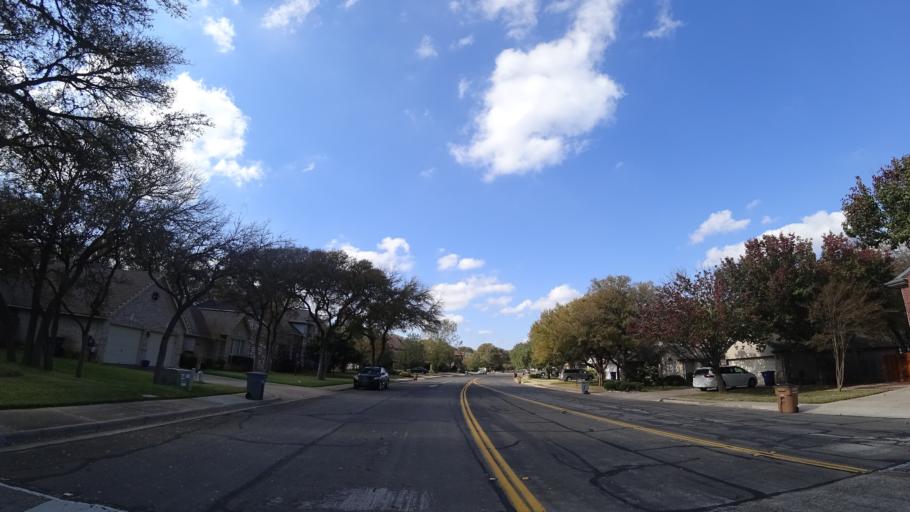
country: US
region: Texas
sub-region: Travis County
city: Shady Hollow
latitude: 30.1805
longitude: -97.8548
